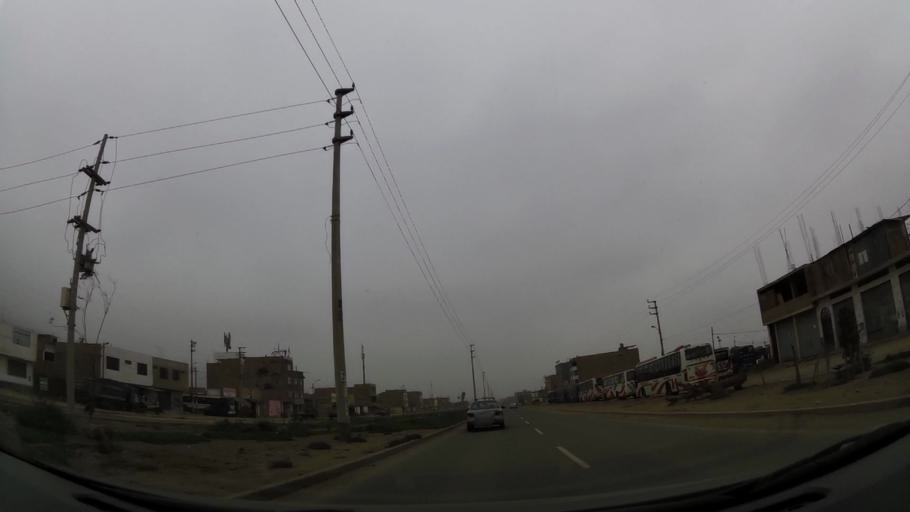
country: PE
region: Lima
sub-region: Lima
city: Urb. Santo Domingo
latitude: -11.8746
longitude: -77.0234
